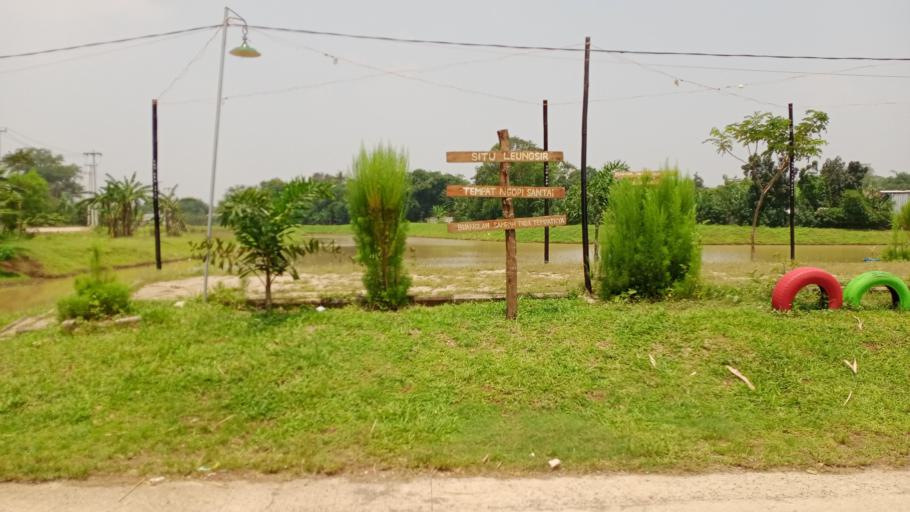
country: ID
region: West Java
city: Cileungsir
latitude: -6.3888
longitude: 107.0738
